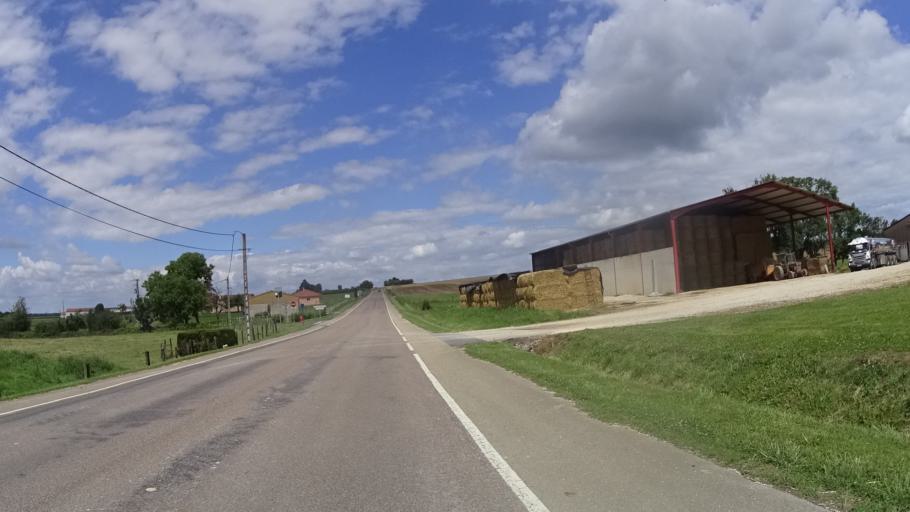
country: FR
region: Champagne-Ardenne
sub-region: Departement de la Haute-Marne
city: Montier-en-Der
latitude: 48.4874
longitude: 4.7594
